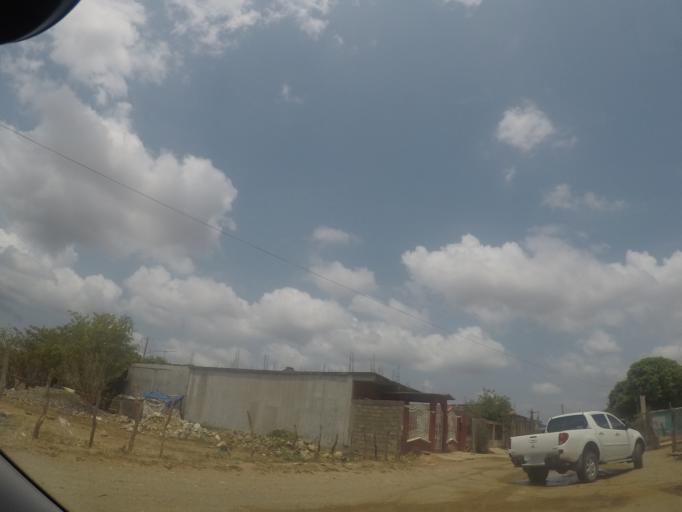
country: MX
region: Oaxaca
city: El Espinal
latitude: 16.5514
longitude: -94.9427
